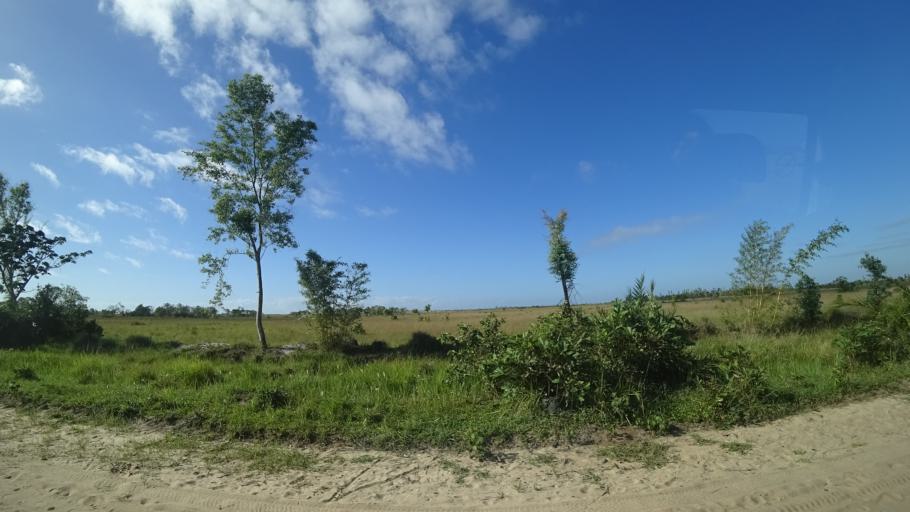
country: MZ
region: Sofala
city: Beira
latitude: -19.7221
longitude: 34.9972
